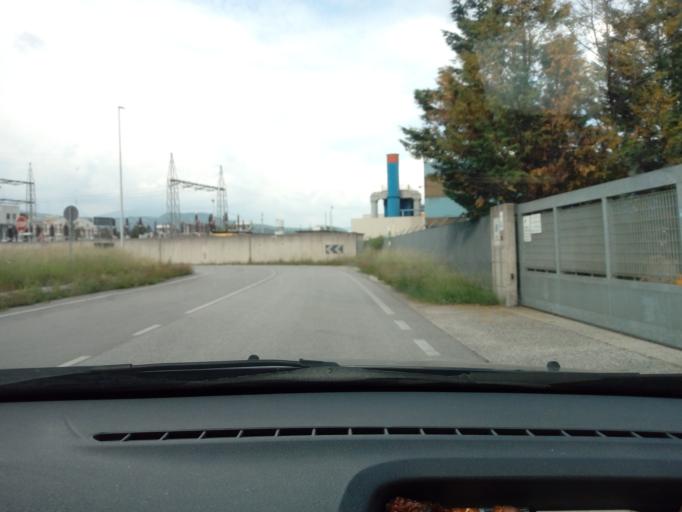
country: IT
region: Friuli Venezia Giulia
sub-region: Provincia di Udine
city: Moimacco
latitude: 46.0869
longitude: 13.3939
